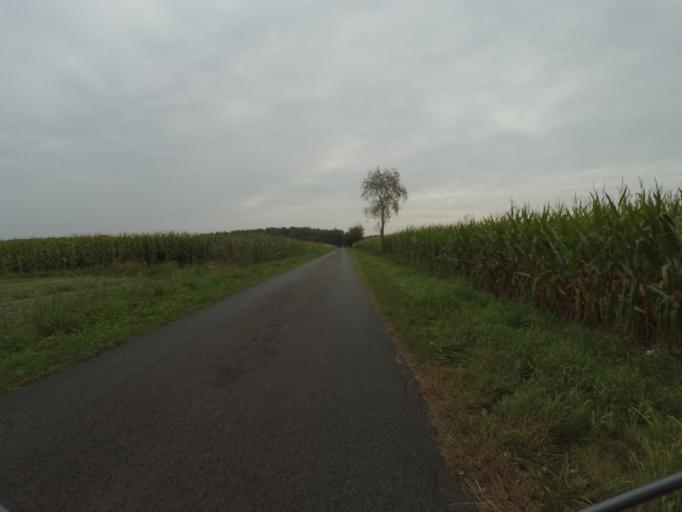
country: NL
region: Overijssel
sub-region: Gemeente Losser
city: Losser
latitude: 52.2764
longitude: 7.0649
